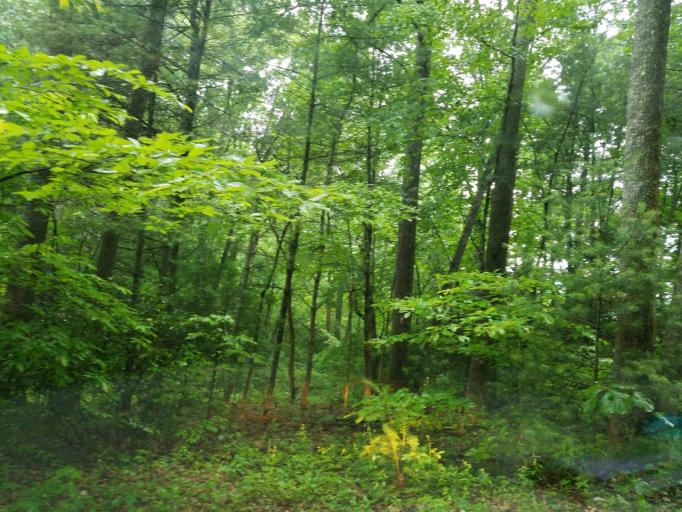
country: US
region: Georgia
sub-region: Lumpkin County
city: Dahlonega
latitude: 34.6943
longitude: -84.0715
